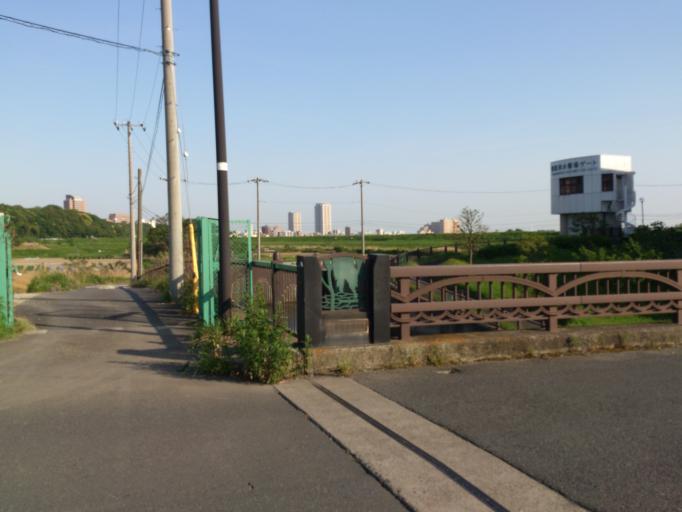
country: JP
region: Chiba
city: Matsudo
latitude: 35.7522
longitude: 139.8922
